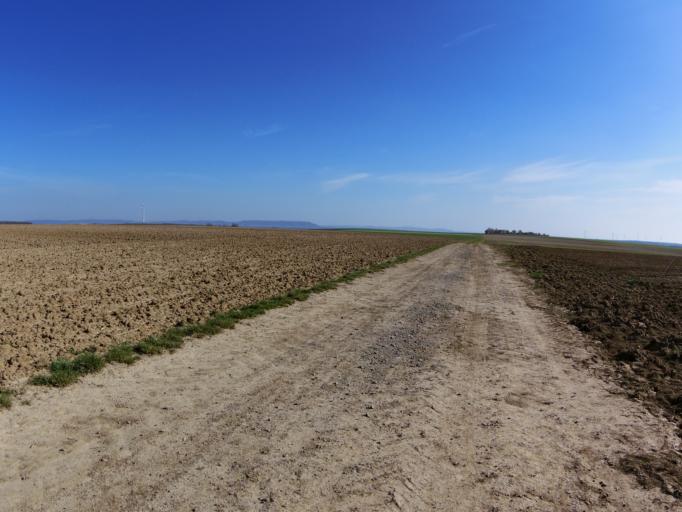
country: DE
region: Bavaria
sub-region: Regierungsbezirk Unterfranken
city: Prosselsheim
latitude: 49.8503
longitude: 10.1170
